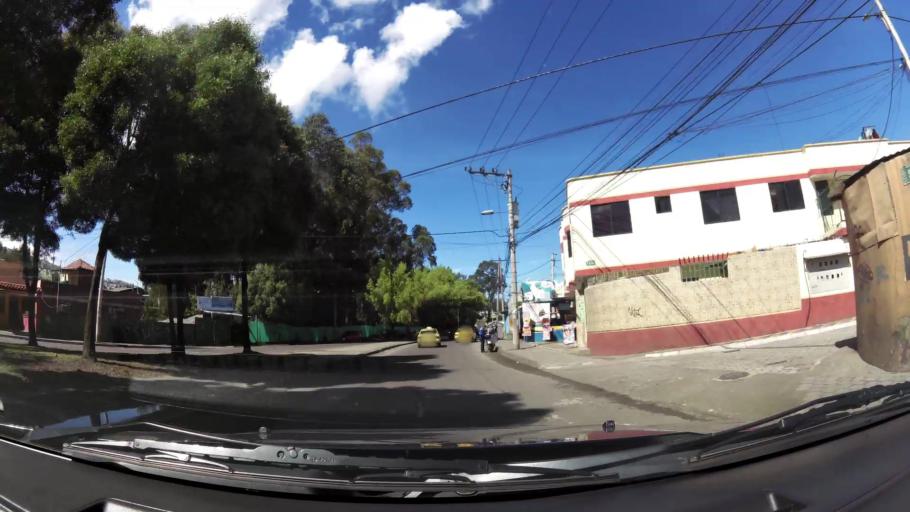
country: EC
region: Pichincha
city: Quito
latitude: -0.2880
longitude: -78.5415
